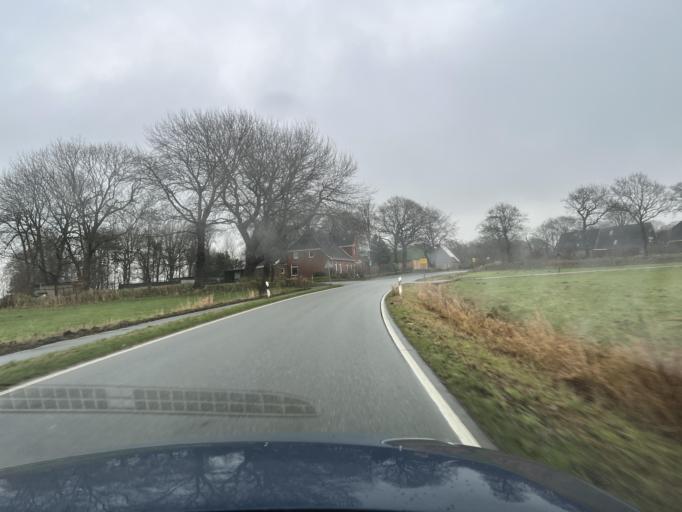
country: DE
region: Schleswig-Holstein
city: Lohe-Rickelshof
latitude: 54.2200
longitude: 9.0598
